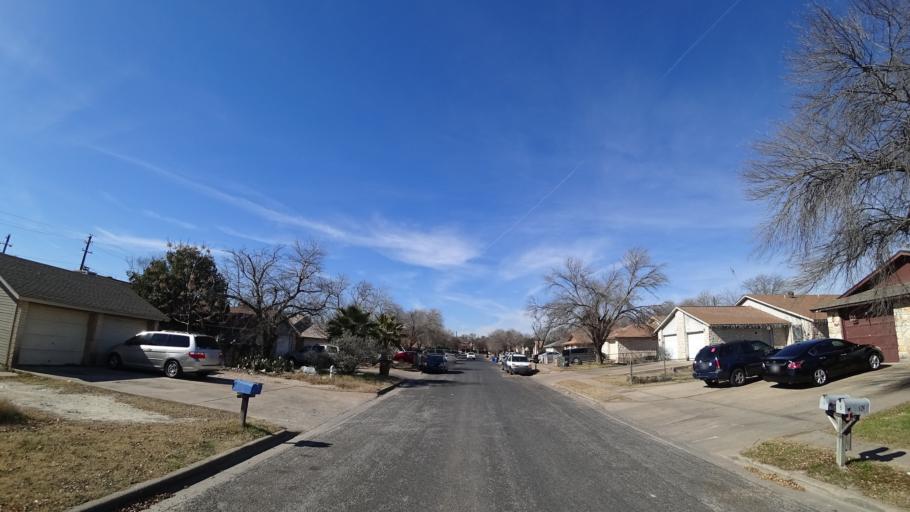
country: US
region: Texas
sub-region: Travis County
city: Wells Branch
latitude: 30.3706
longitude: -97.6977
